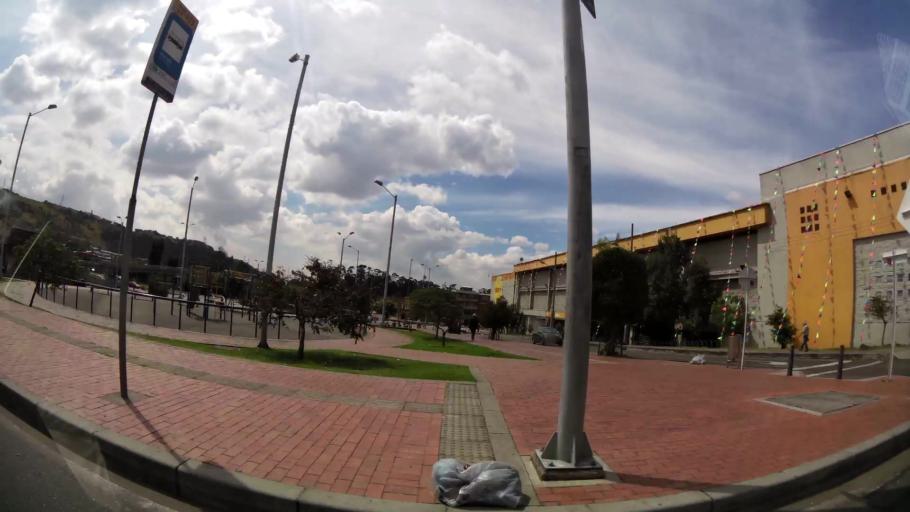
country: CO
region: Bogota D.C.
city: Bogota
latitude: 4.5684
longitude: -74.0998
